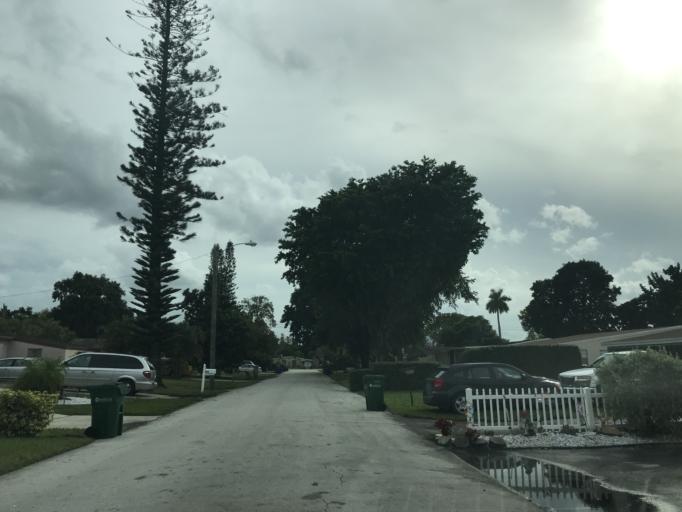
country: US
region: Florida
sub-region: Broward County
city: Margate
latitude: 26.2598
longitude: -80.2063
